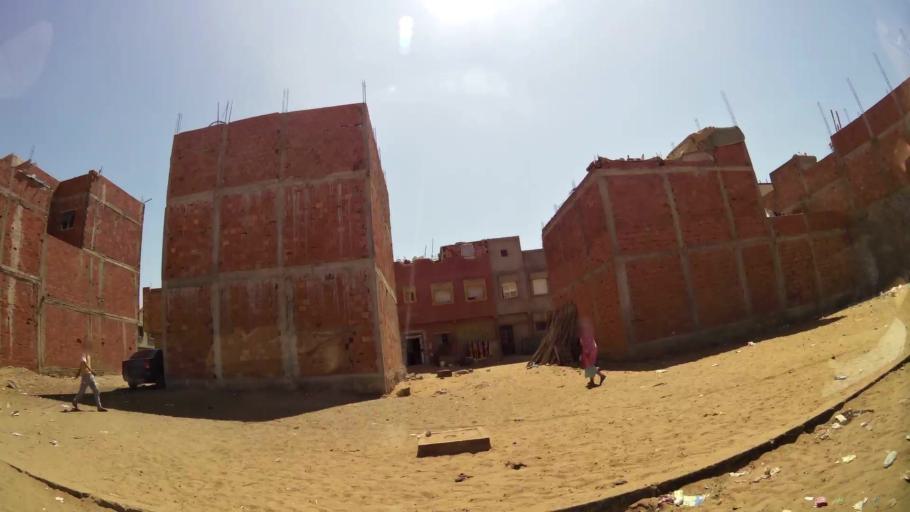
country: MA
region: Gharb-Chrarda-Beni Hssen
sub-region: Kenitra Province
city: Kenitra
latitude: 34.2274
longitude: -6.5489
